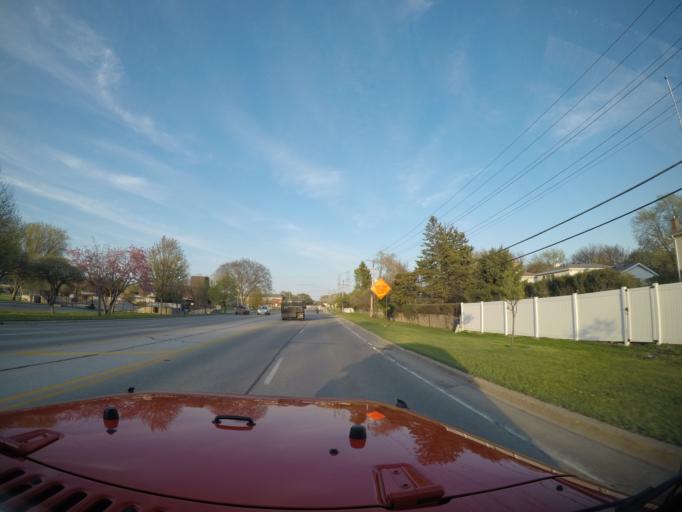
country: US
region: Illinois
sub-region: Cook County
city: Prospect Heights
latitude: 42.0878
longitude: -87.9105
